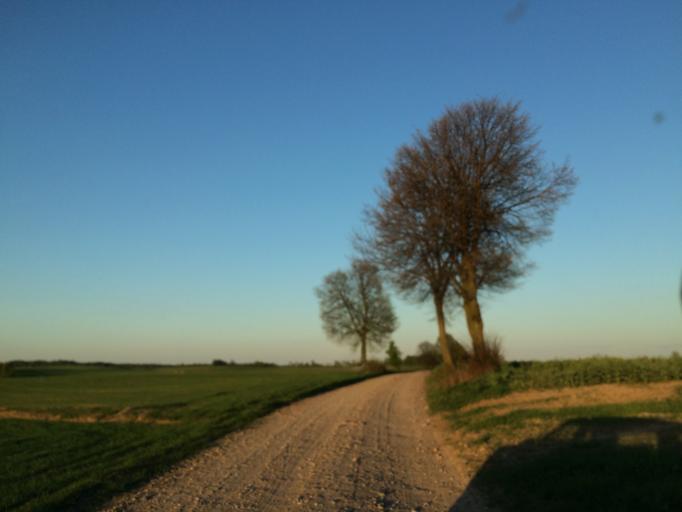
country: PL
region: Warmian-Masurian Voivodeship
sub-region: Powiat dzialdowski
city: Rybno
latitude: 53.4740
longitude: 19.8854
